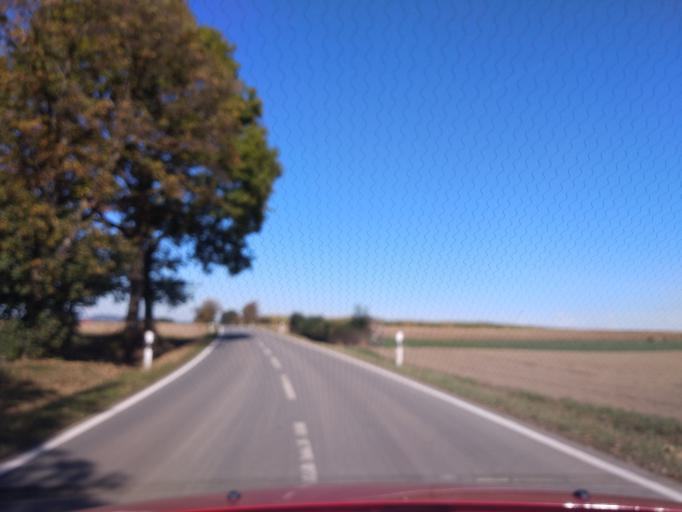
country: DE
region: Lower Saxony
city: Boffzen
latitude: 51.7426
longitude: 9.3040
